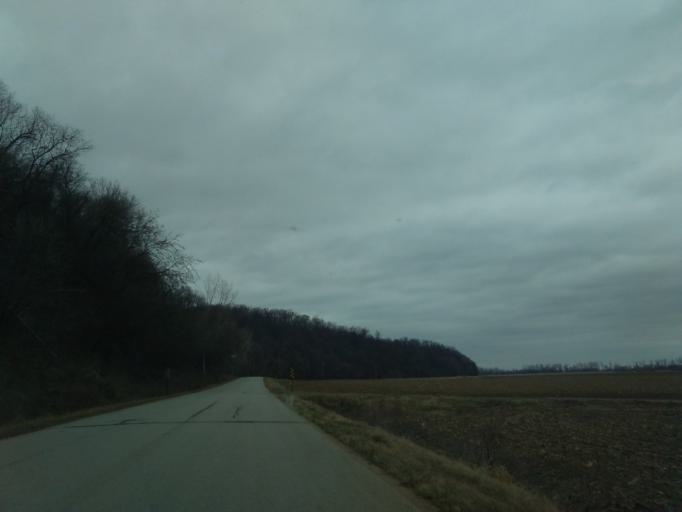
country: US
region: Kansas
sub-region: Doniphan County
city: Highland
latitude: 40.0029
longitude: -95.3338
